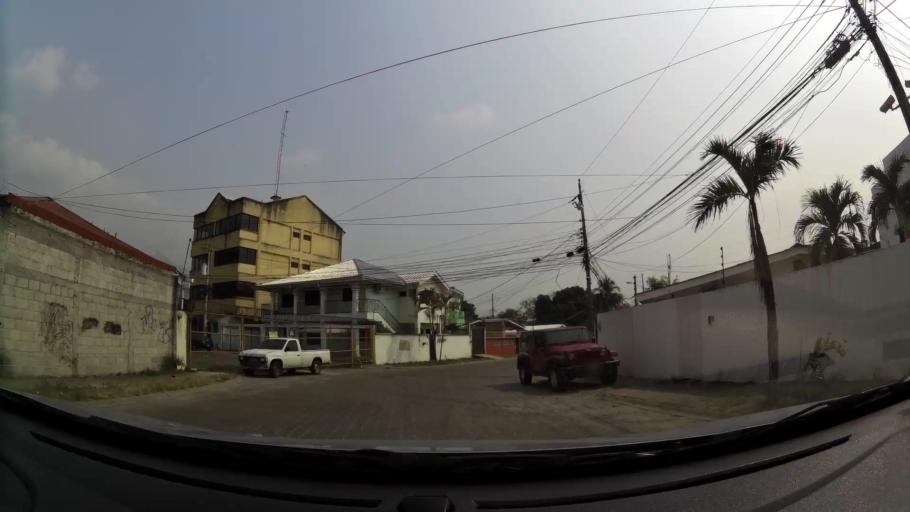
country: HN
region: Cortes
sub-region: San Pedro Sula
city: Pena Blanca
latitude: 15.5274
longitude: -88.0312
